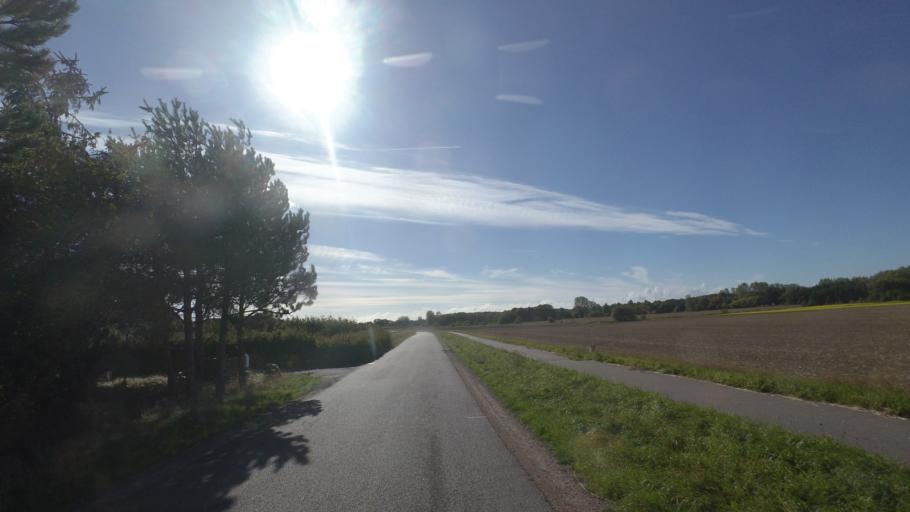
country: DK
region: Capital Region
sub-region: Bornholm Kommune
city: Akirkeby
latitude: 55.0147
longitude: 14.9916
